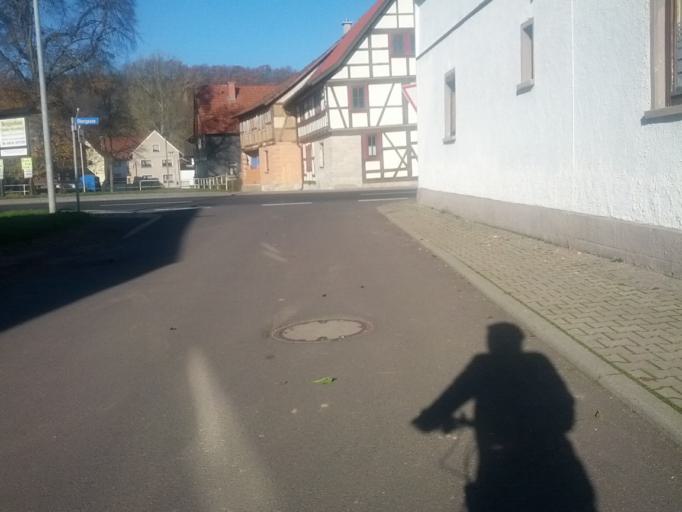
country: DE
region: Thuringia
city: Mechterstadt
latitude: 50.9438
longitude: 10.4802
